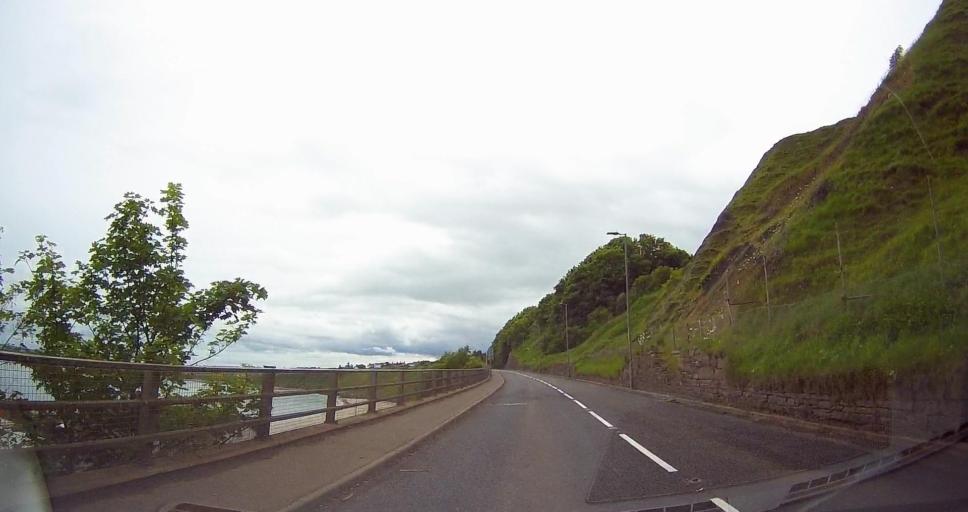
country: GB
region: Scotland
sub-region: Highland
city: Thurso
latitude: 58.6093
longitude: -3.5524
